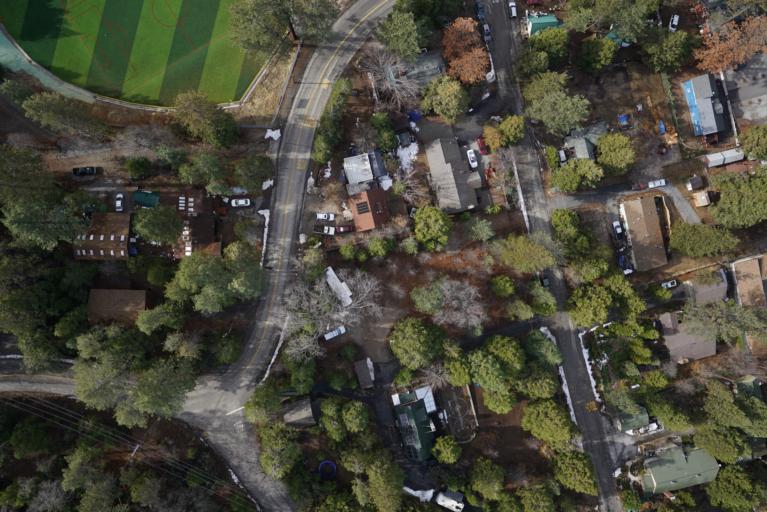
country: US
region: California
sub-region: Riverside County
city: Idyllwild
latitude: 33.7382
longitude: -116.7190
